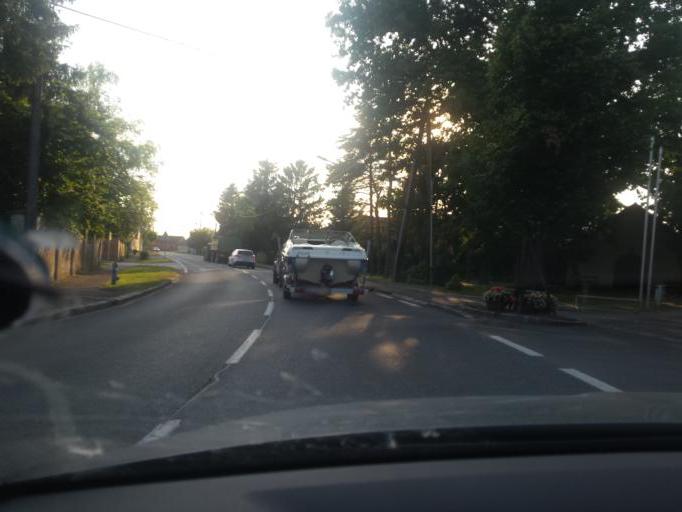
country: AT
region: Lower Austria
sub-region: Politischer Bezirk Bruck an der Leitha
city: Rohrau
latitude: 48.0486
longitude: 16.8367
